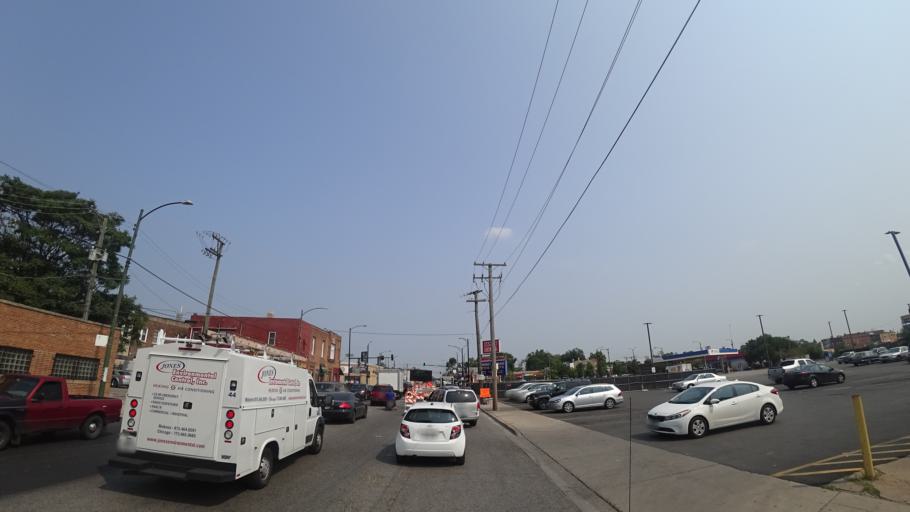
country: US
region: Illinois
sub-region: Cook County
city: Cicero
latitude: 41.8504
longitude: -87.7247
